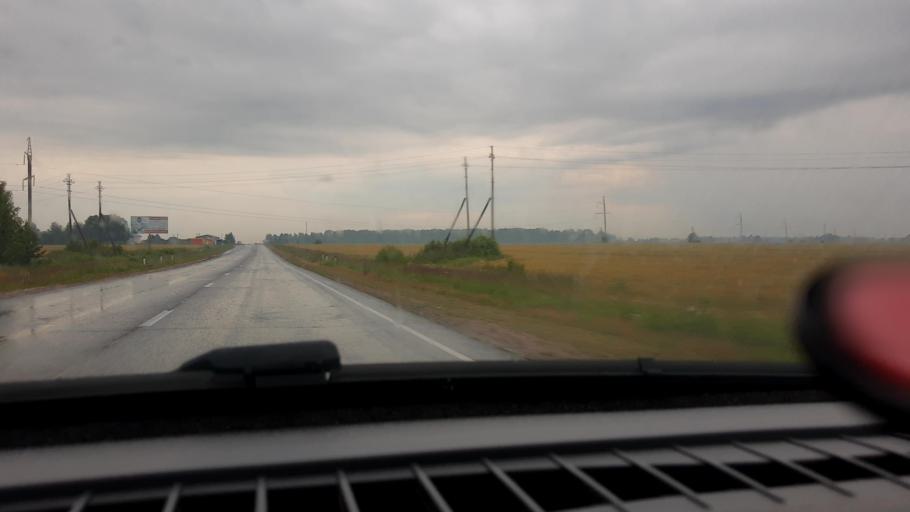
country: RU
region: Nizjnij Novgorod
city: Gorodets
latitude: 56.6571
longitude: 43.5025
